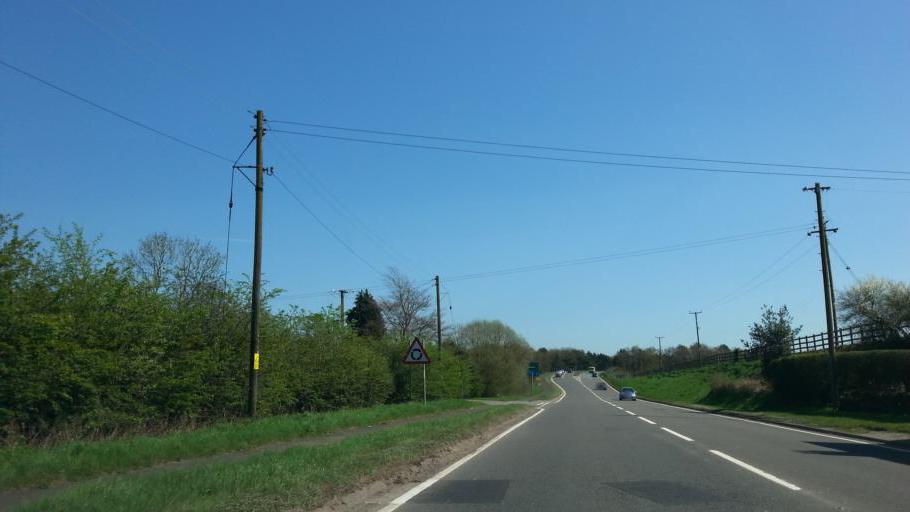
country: GB
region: England
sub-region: Staffordshire
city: Penkridge
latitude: 52.6901
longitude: -2.1106
